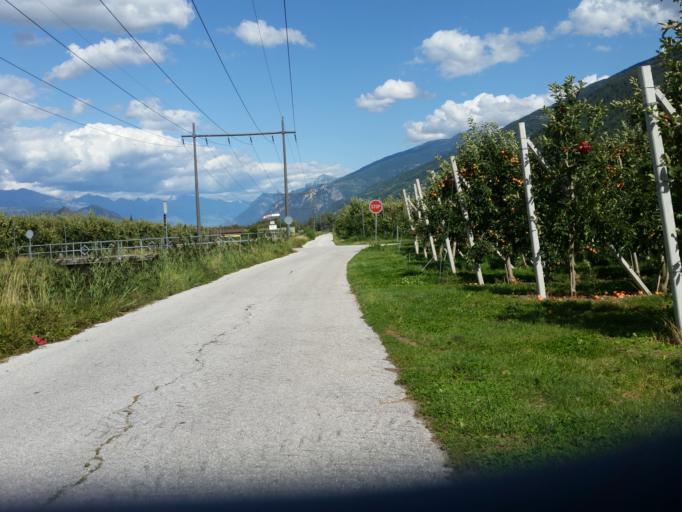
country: CH
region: Valais
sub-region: Conthey District
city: Ardon
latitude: 46.1990
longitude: 7.2664
